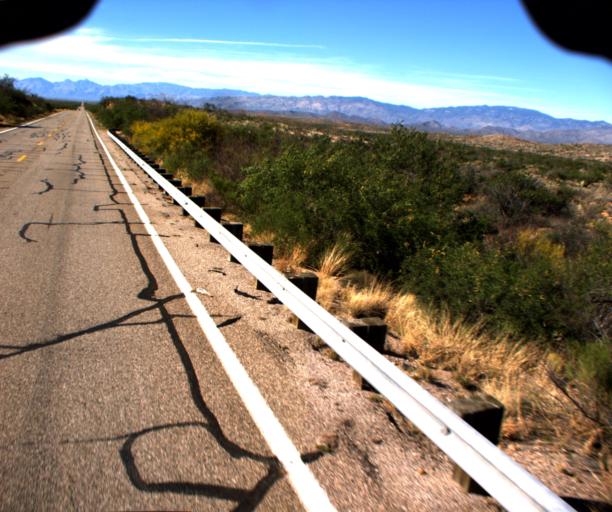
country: US
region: Arizona
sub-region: Pima County
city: Corona de Tucson
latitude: 31.9352
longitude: -110.6605
